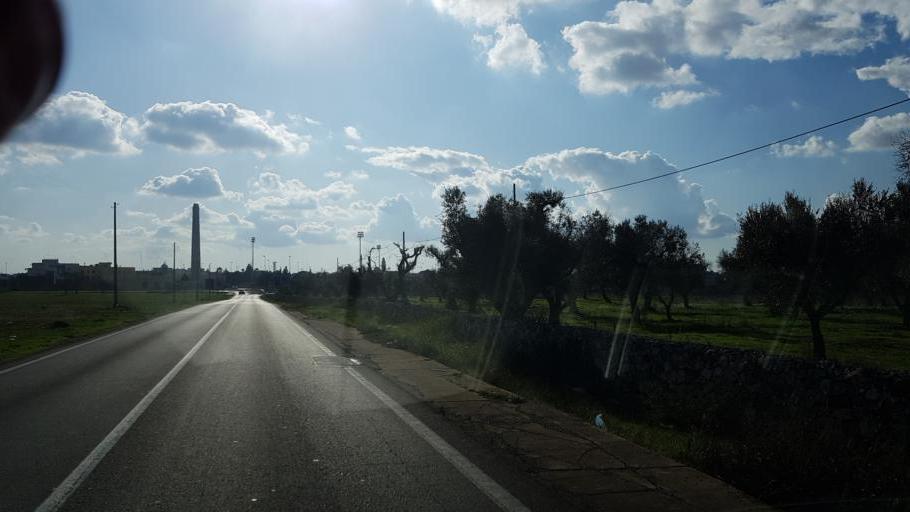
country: IT
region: Apulia
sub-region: Provincia di Lecce
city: Campi Salentina
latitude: 40.4090
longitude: 18.0224
